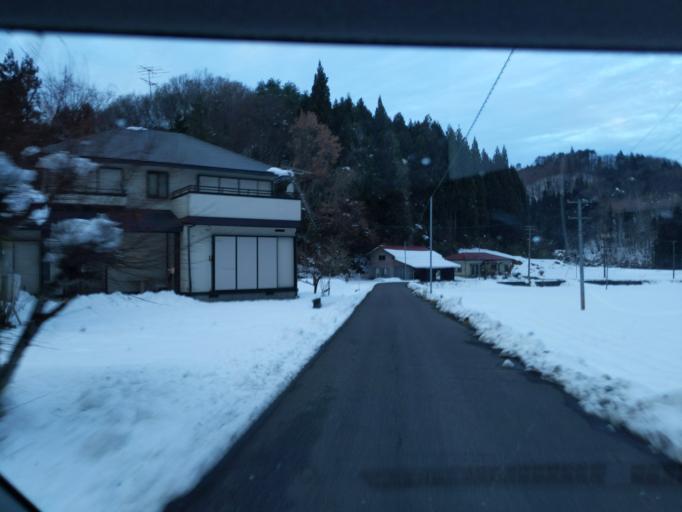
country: JP
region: Iwate
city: Mizusawa
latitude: 39.0451
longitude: 141.0123
